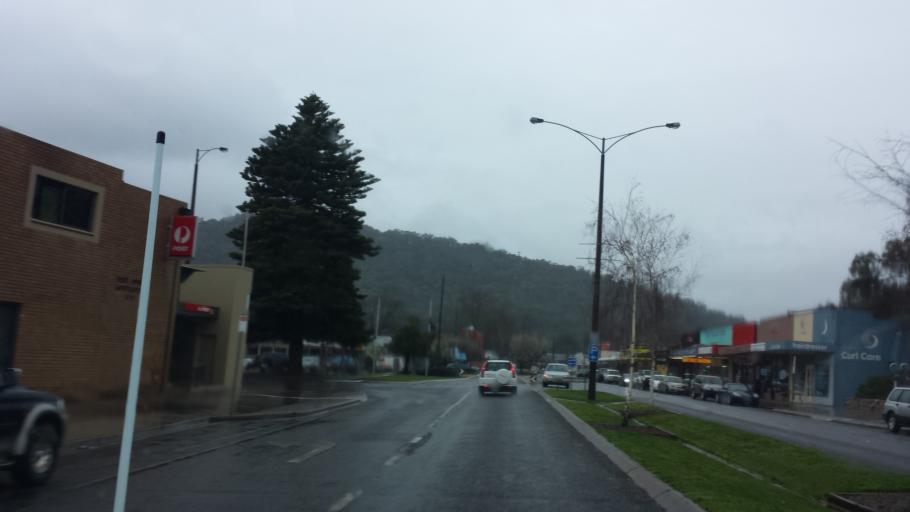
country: AU
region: Victoria
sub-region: Wangaratta
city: Wangaratta
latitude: -36.5617
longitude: 146.7254
